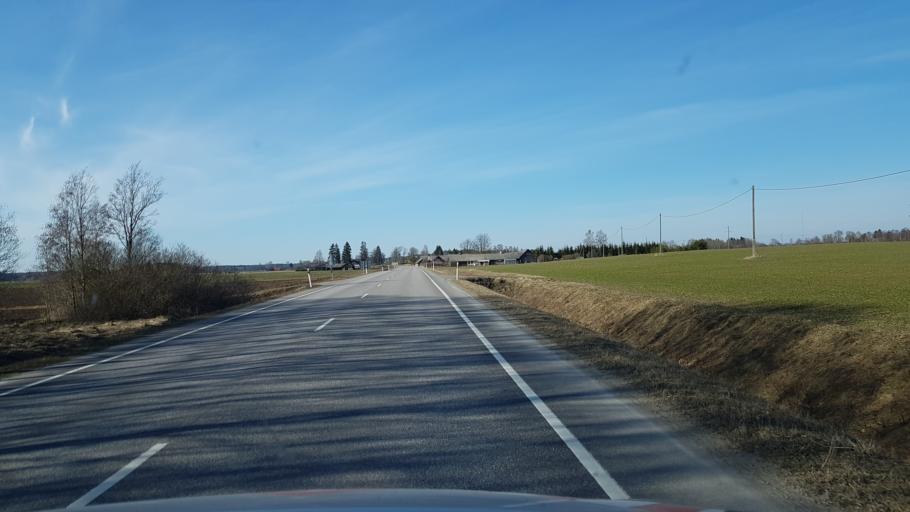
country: EE
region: Laeaene-Virumaa
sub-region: Vinni vald
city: Vinni
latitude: 59.1431
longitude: 26.5961
